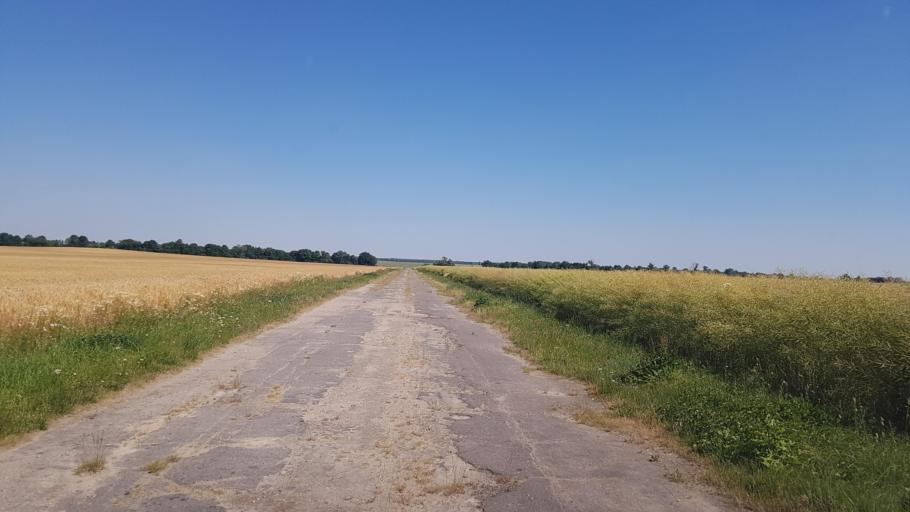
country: DE
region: Saxony-Anhalt
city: Seyda
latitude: 51.9656
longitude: 12.8912
